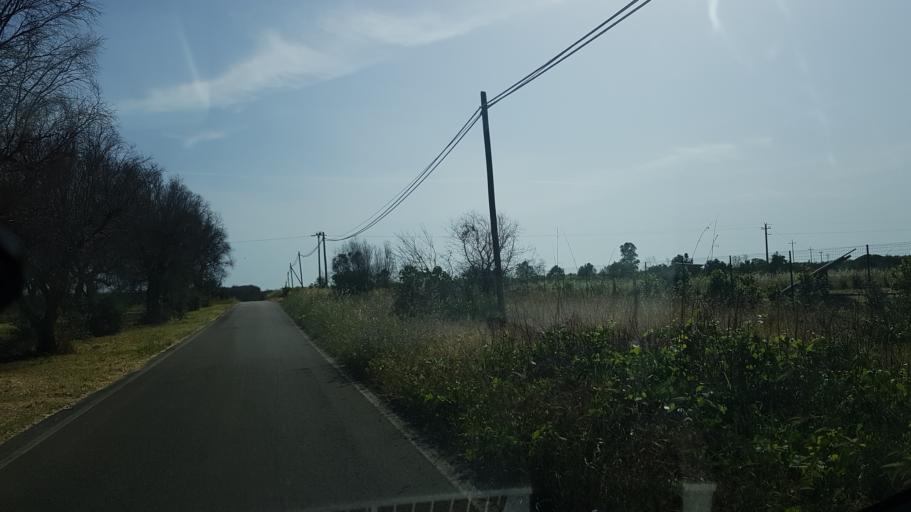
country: IT
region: Apulia
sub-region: Provincia di Brindisi
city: Torchiarolo
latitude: 40.5105
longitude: 18.0741
